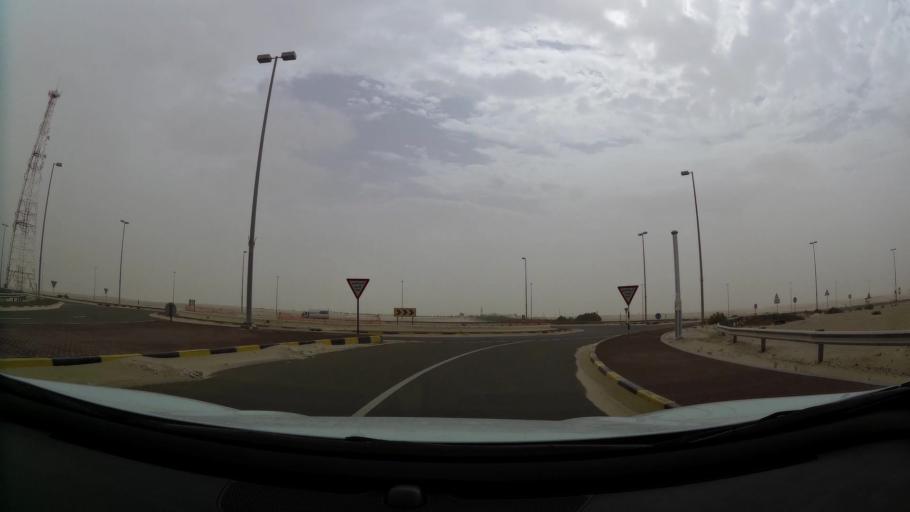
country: AE
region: Abu Dhabi
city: Abu Dhabi
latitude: 24.3537
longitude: 54.7104
